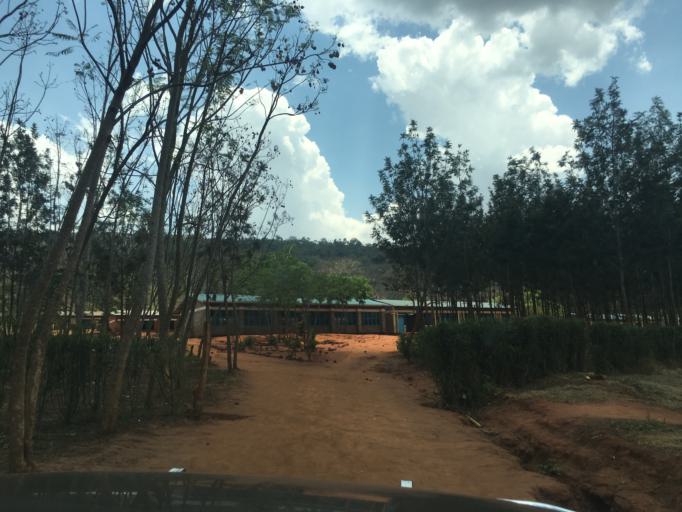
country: RW
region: Eastern Province
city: Kibungo
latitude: -2.1159
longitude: 30.8477
